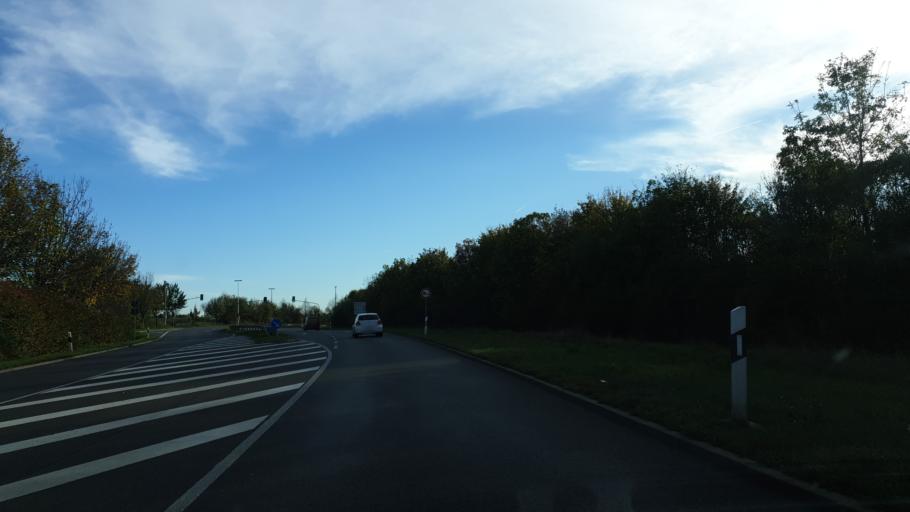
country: DE
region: Thuringia
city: Gera
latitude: 50.8690
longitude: 12.1141
